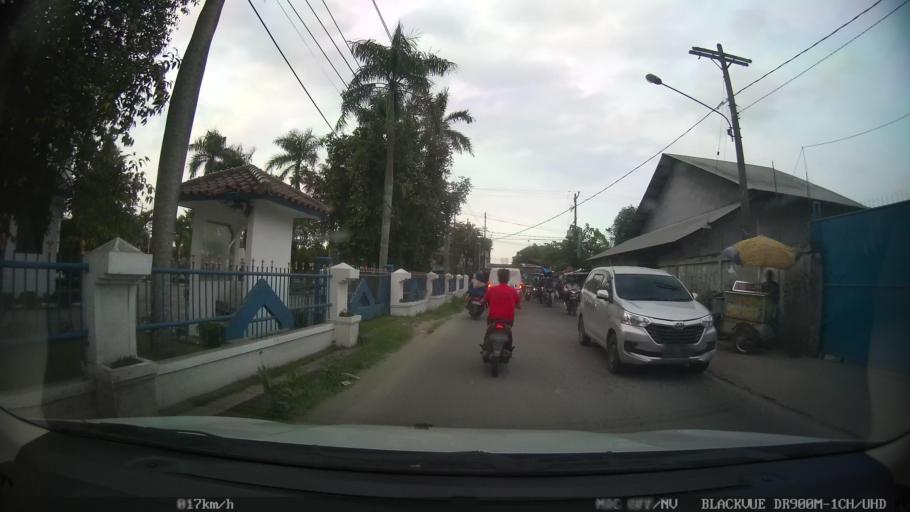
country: ID
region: North Sumatra
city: Sunggal
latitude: 3.5684
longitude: 98.6119
